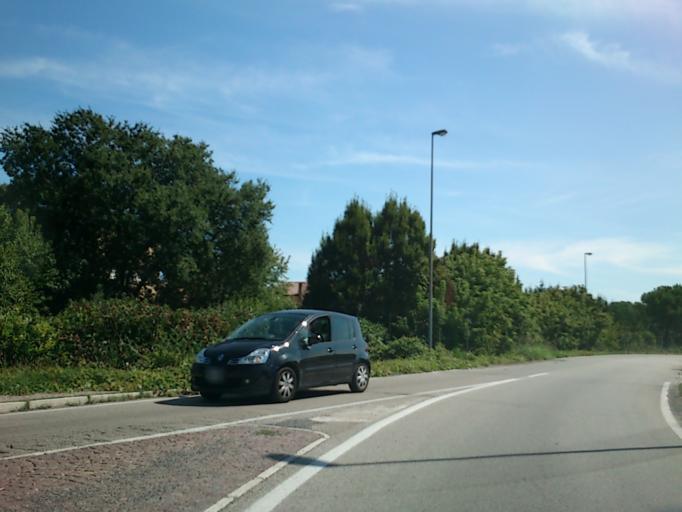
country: IT
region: Emilia-Romagna
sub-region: Provincia di Rimini
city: Cattolica
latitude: 43.9570
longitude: 12.7301
